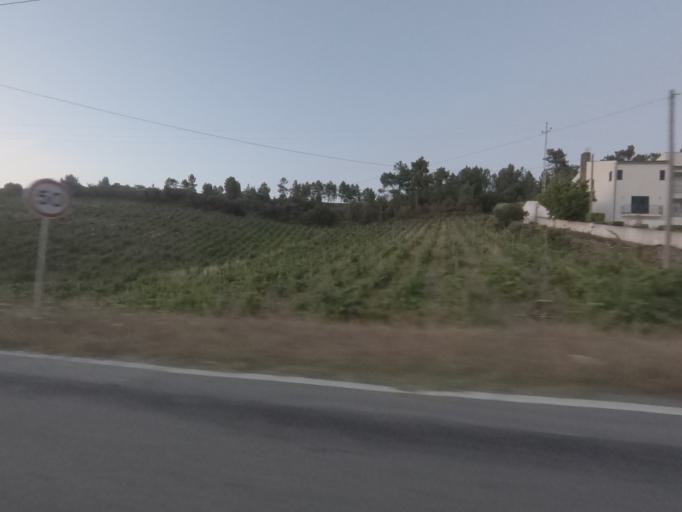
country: PT
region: Viseu
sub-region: Armamar
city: Armamar
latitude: 41.2011
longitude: -7.6982
